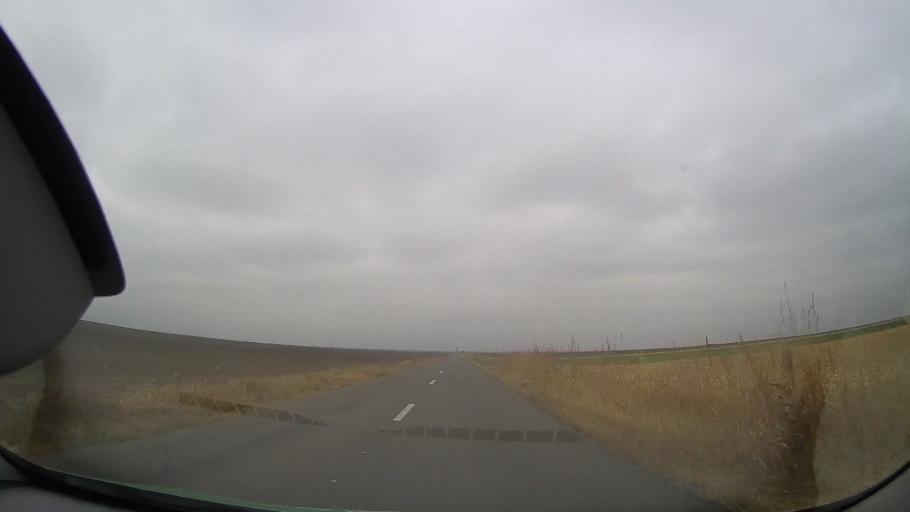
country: RO
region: Buzau
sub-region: Comuna Bradeanu
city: Bradeanu
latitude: 44.8893
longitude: 26.8747
